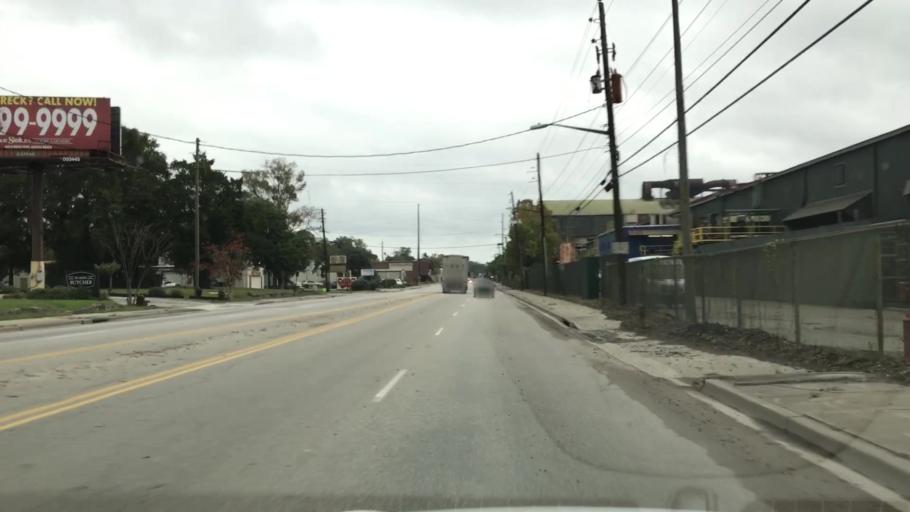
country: US
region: South Carolina
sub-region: Georgetown County
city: Georgetown
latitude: 33.3669
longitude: -79.2937
